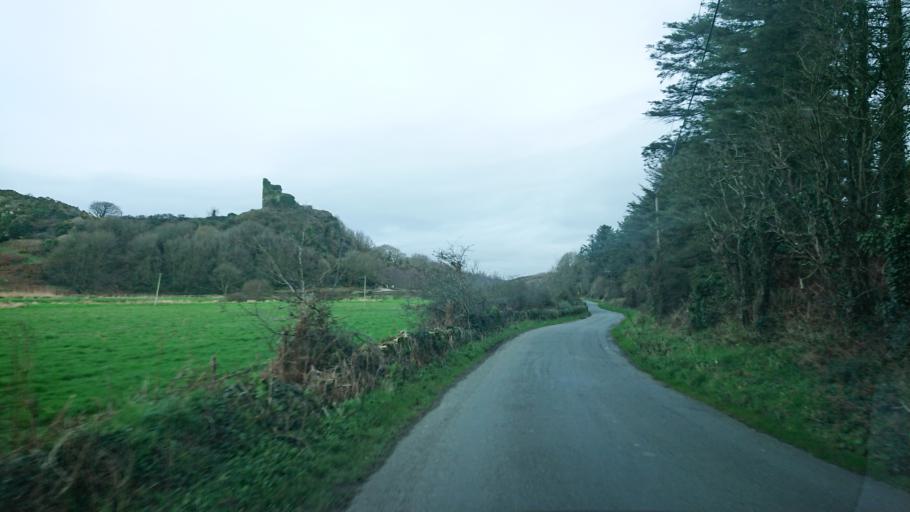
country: IE
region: Munster
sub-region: Waterford
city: Tra Mhor
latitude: 52.1551
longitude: -7.2619
